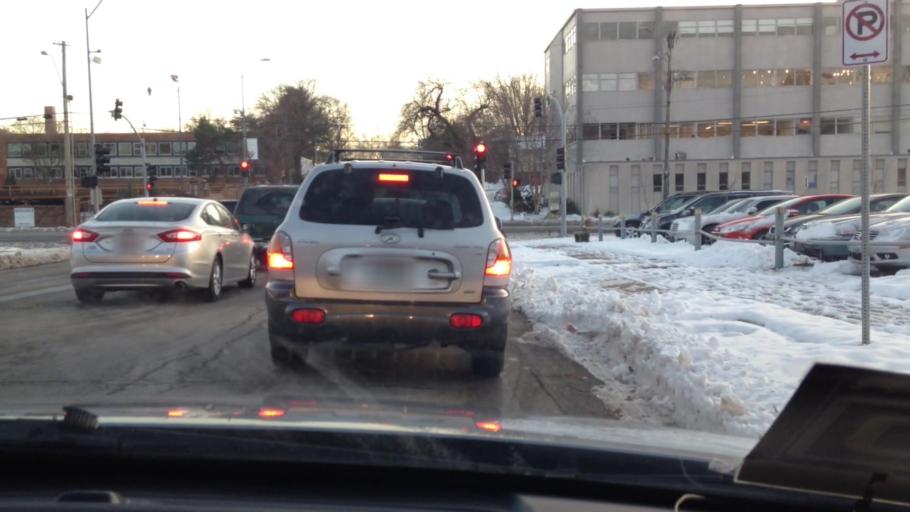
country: US
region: Kansas
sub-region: Johnson County
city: Mission Hills
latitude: 39.0139
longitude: -94.5769
